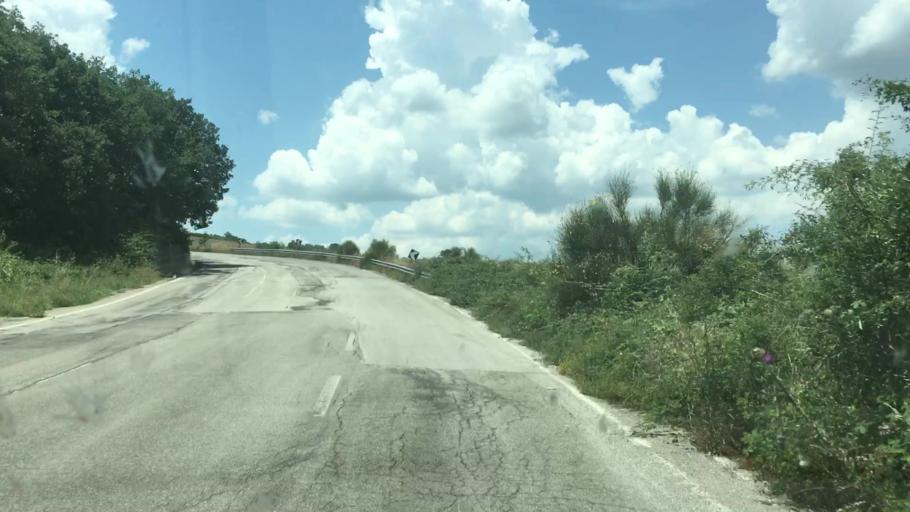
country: IT
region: Basilicate
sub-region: Provincia di Potenza
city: Tolve
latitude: 40.6864
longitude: 15.9804
